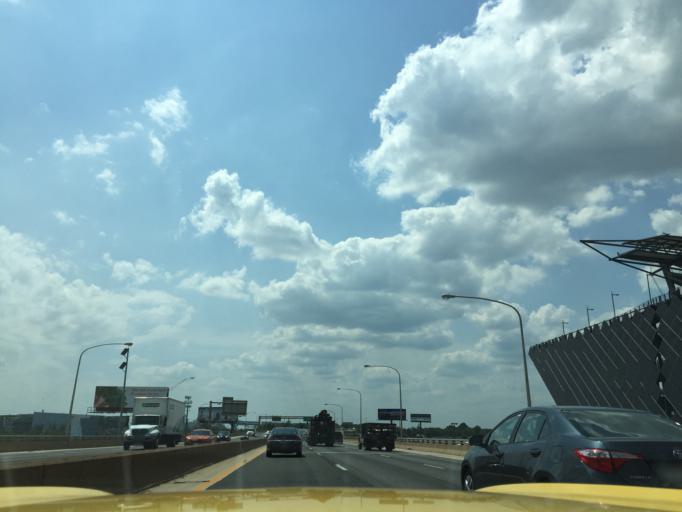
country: US
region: New Jersey
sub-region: Gloucester County
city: National Park
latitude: 39.8992
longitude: -75.1665
